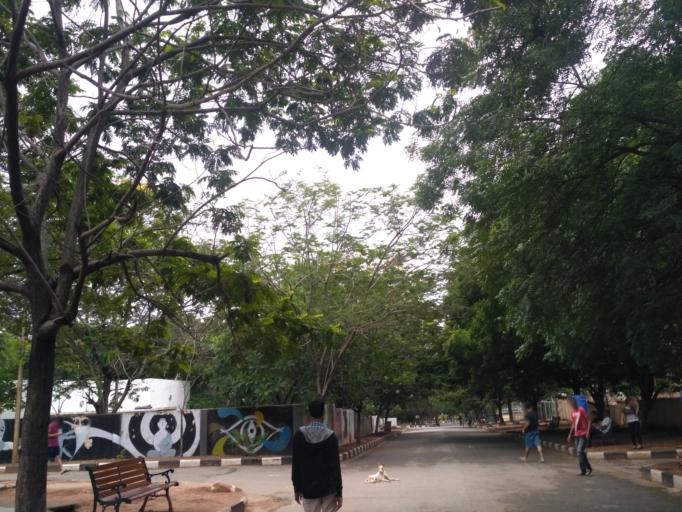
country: IN
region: Telangana
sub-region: Medak
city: Serilingampalle
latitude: 17.4470
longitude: 78.3478
